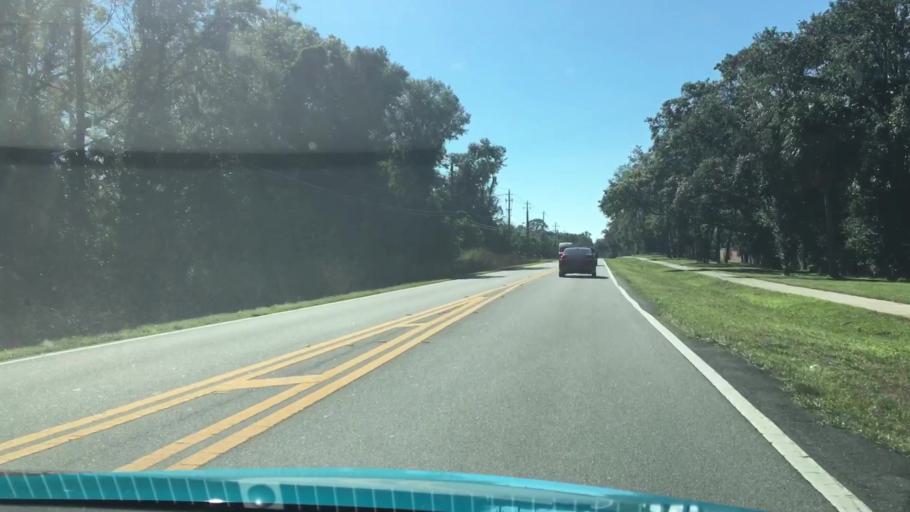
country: US
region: Florida
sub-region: Seminole County
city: Heathrow
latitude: 28.7907
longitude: -81.3630
